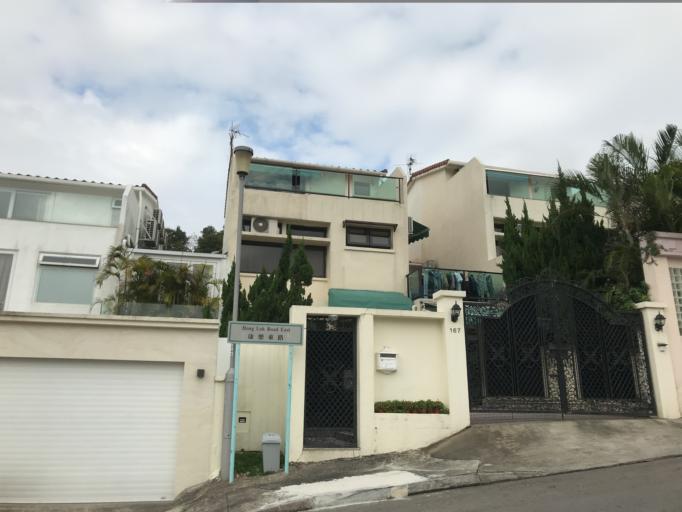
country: HK
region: Tai Po
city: Tai Po
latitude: 22.4653
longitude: 114.1574
